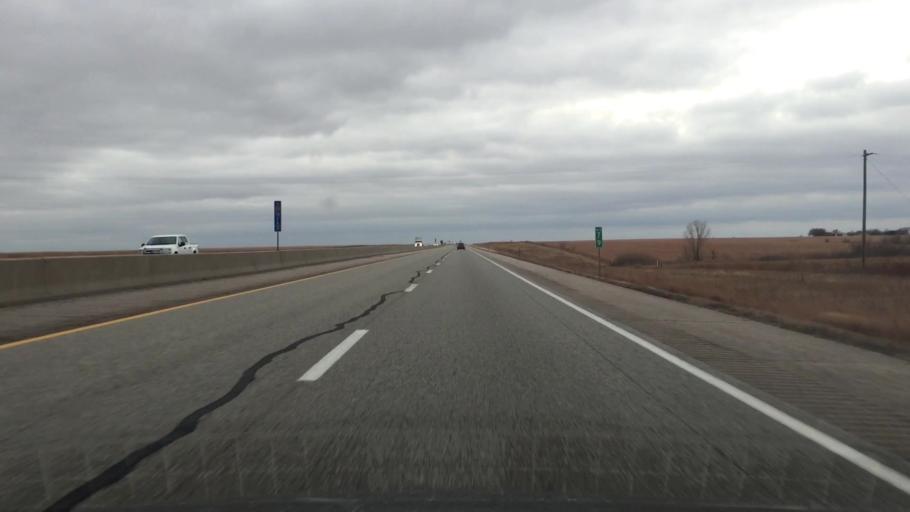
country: US
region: Kansas
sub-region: Butler County
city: El Dorado
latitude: 37.9116
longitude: -96.8091
